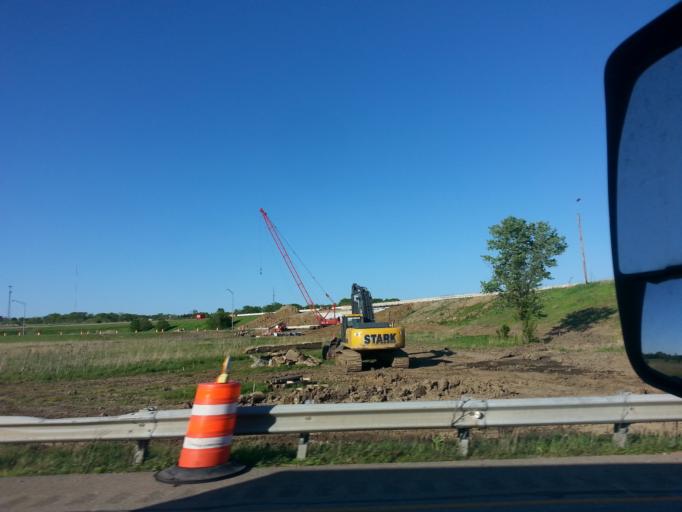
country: US
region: Illinois
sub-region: McLean County
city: Bloomington
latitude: 40.4414
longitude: -89.0200
